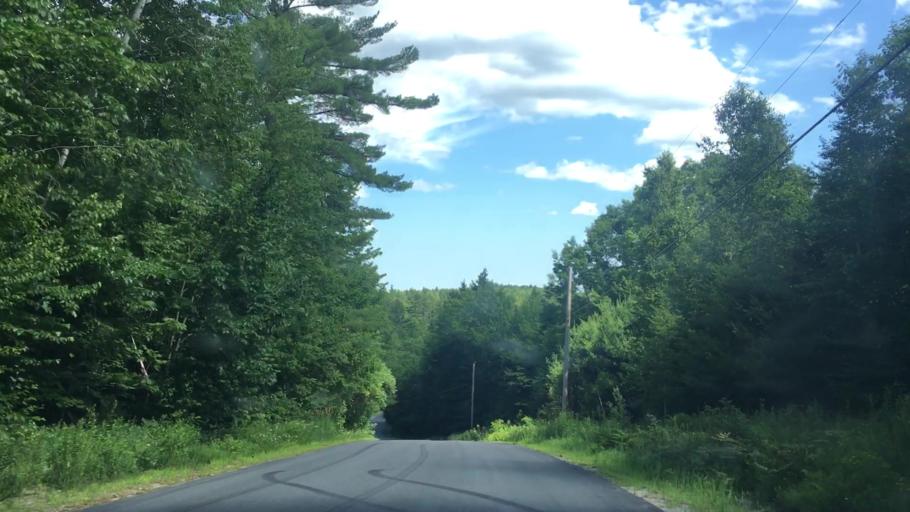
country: US
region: Maine
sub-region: Franklin County
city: Chesterville
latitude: 44.5615
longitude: -70.1320
